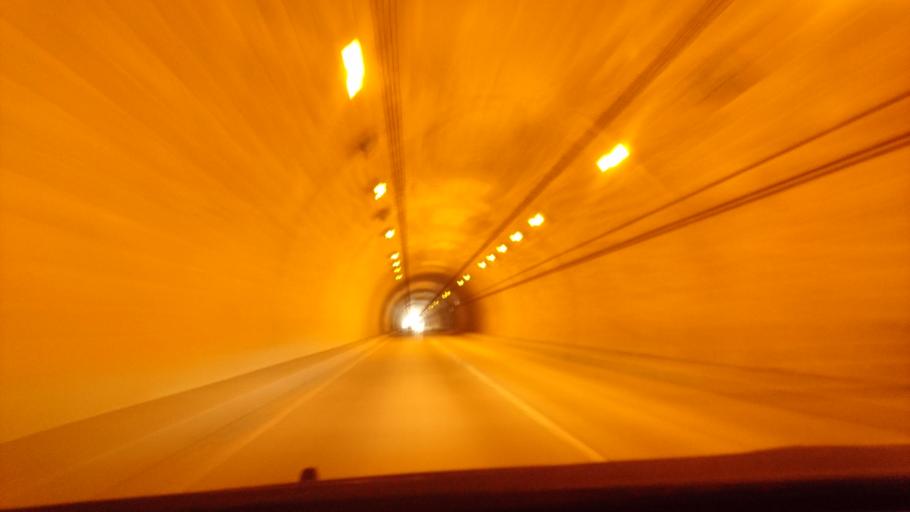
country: JP
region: Miyagi
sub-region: Oshika Gun
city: Onagawa Cho
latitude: 38.5843
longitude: 141.4673
